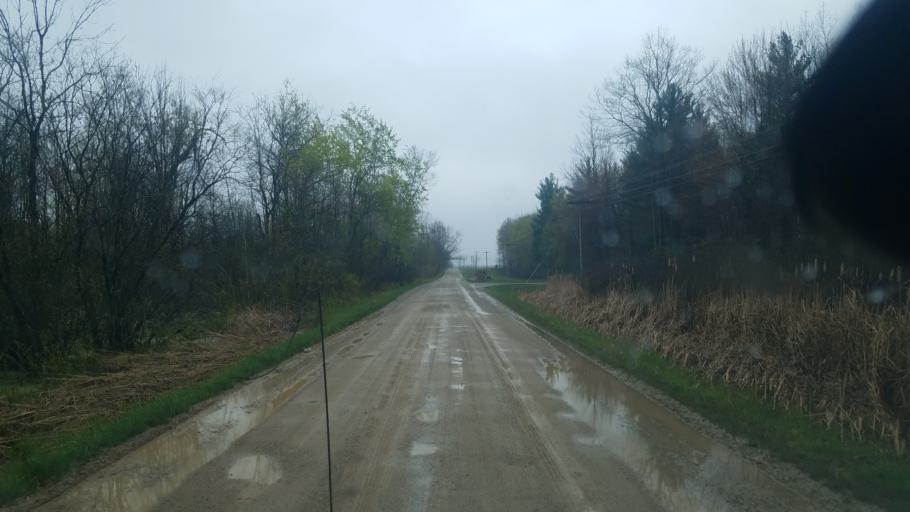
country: US
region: Michigan
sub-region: Montcalm County
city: Lakeview
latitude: 43.4744
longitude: -85.2937
